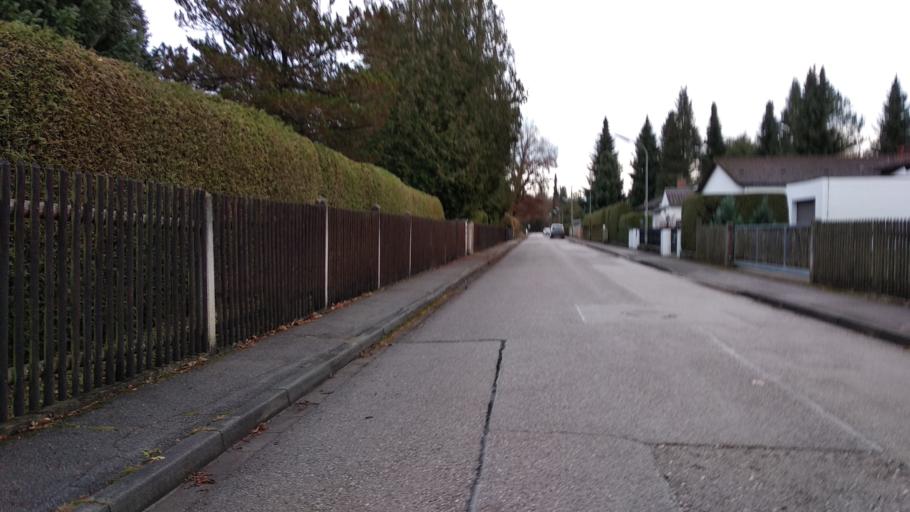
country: DE
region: Bavaria
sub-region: Upper Bavaria
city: Hohenbrunn
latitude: 48.0674
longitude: 11.6914
